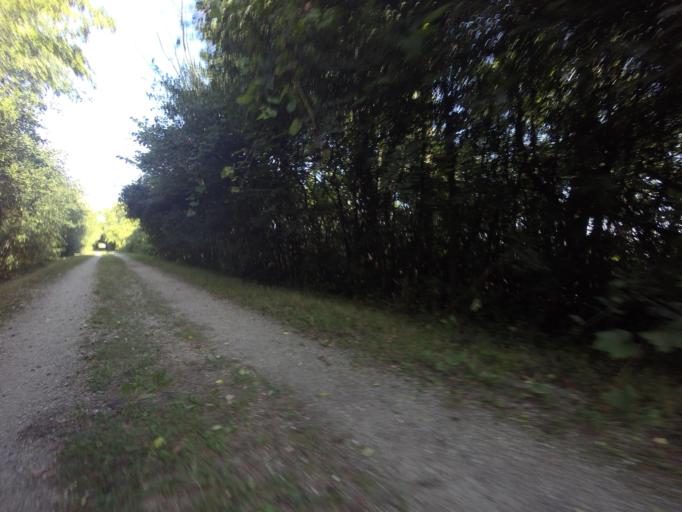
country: CA
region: Ontario
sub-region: Wellington County
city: Guelph
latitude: 43.6572
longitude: -80.4248
